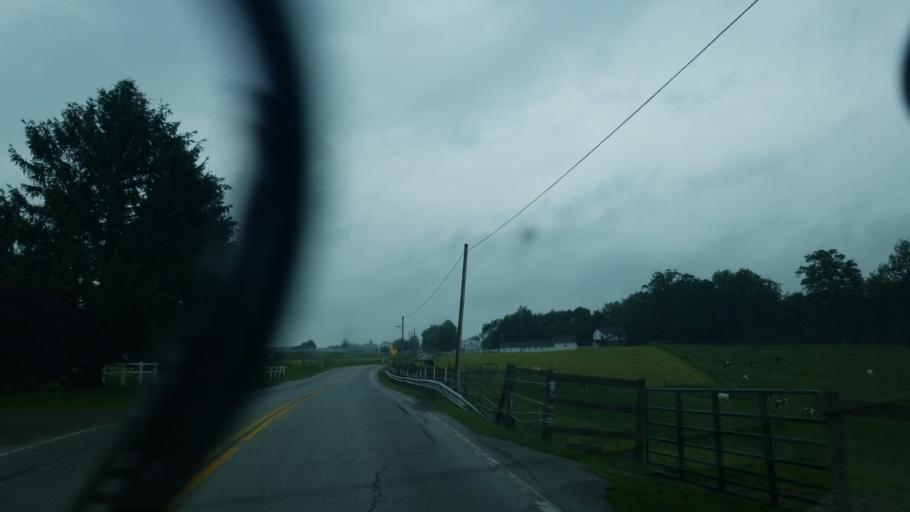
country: US
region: Ohio
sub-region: Tuscarawas County
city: Sugarcreek
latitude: 40.4802
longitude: -81.7227
